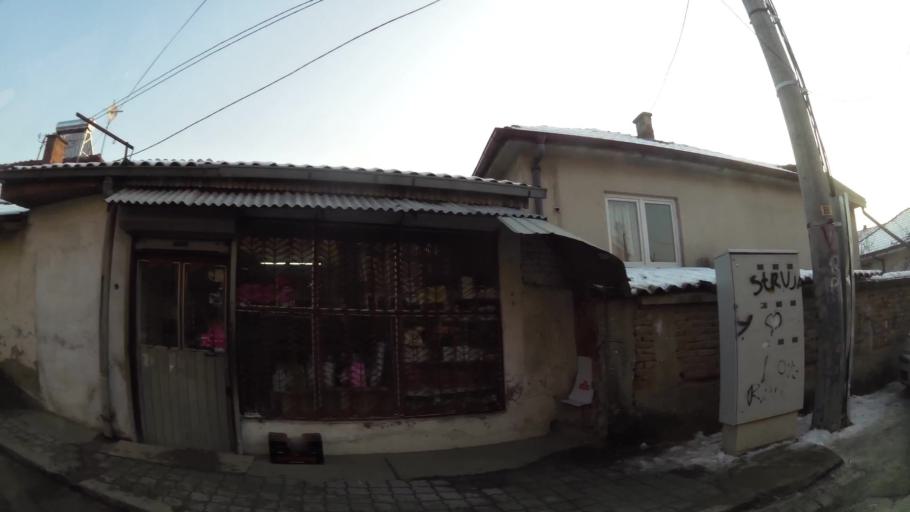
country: MK
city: Creshevo
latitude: 42.0147
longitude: 21.5160
